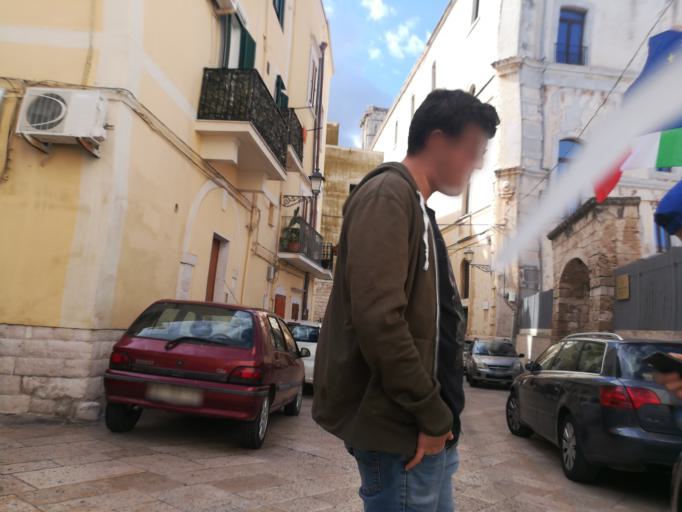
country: IT
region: Apulia
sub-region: Provincia di Bari
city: Bari
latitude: 41.1311
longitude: 16.8688
